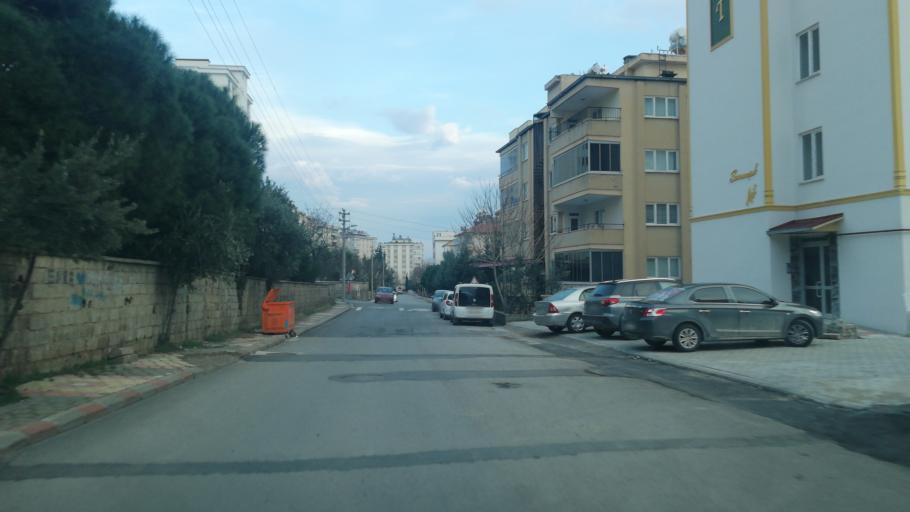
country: TR
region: Kahramanmaras
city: Kahramanmaras
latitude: 37.5867
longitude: 36.8928
